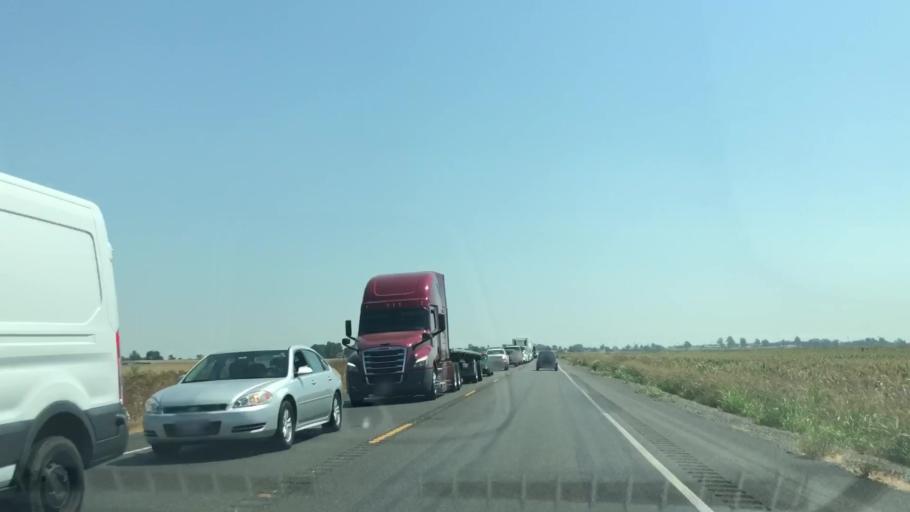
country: US
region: California
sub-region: Solano County
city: Rio Vista
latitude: 38.1356
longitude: -121.6081
